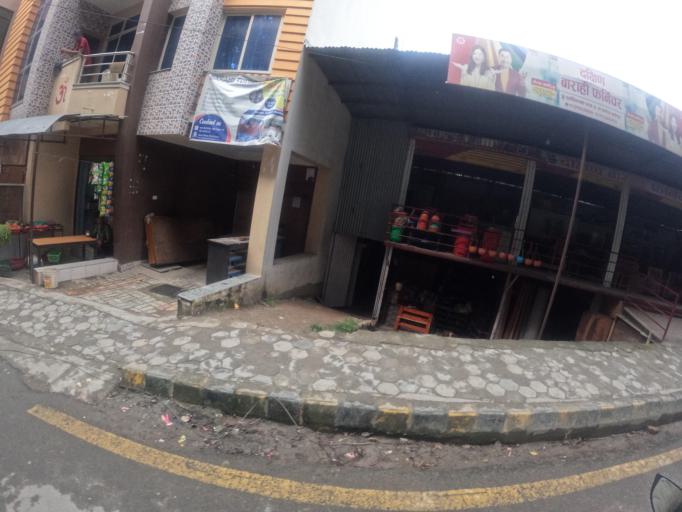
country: NP
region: Central Region
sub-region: Bagmati Zone
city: Bhaktapur
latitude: 27.6655
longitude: 85.3861
